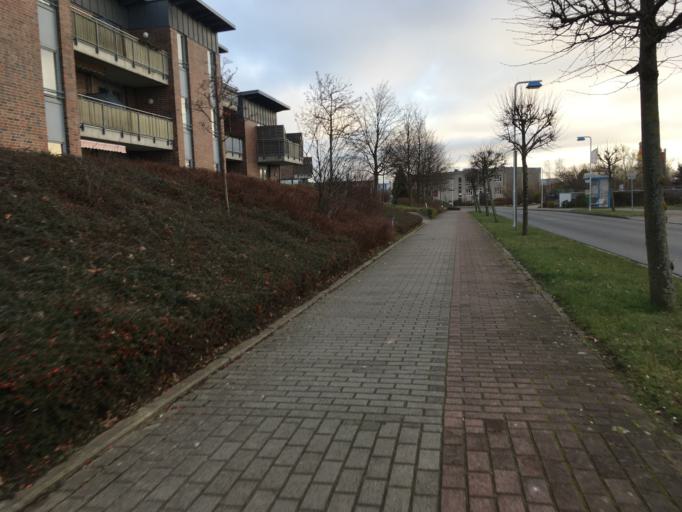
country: DE
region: Mecklenburg-Vorpommern
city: Sassnitz
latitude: 54.5112
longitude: 13.6120
